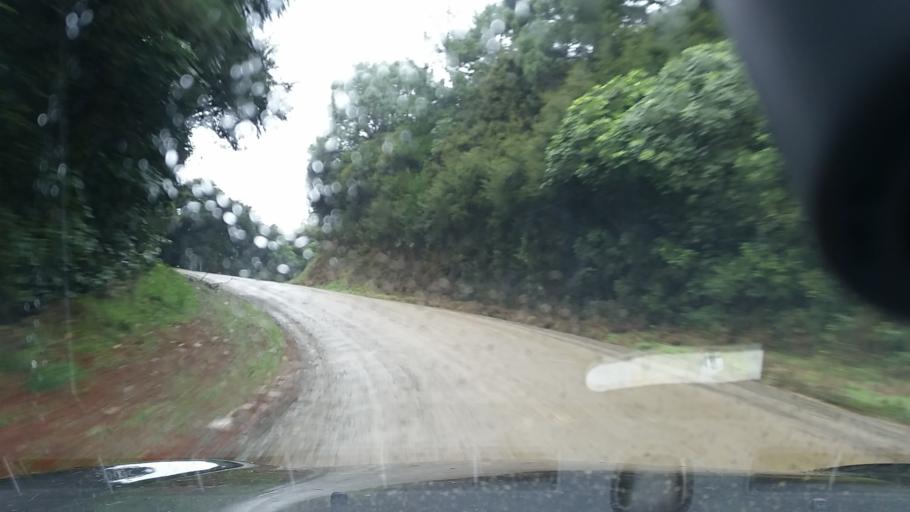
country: NZ
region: Marlborough
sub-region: Marlborough District
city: Picton
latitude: -41.3755
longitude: 174.0640
